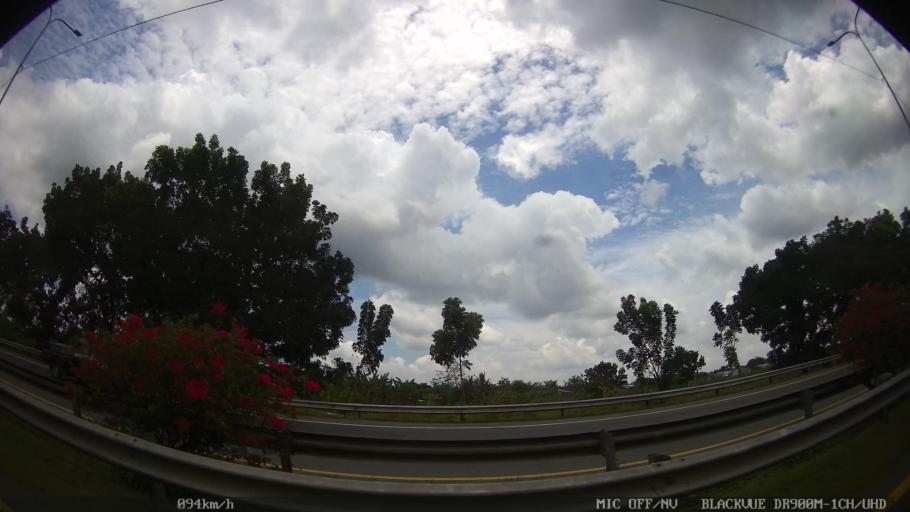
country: ID
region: North Sumatra
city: Medan
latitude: 3.6270
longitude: 98.7190
